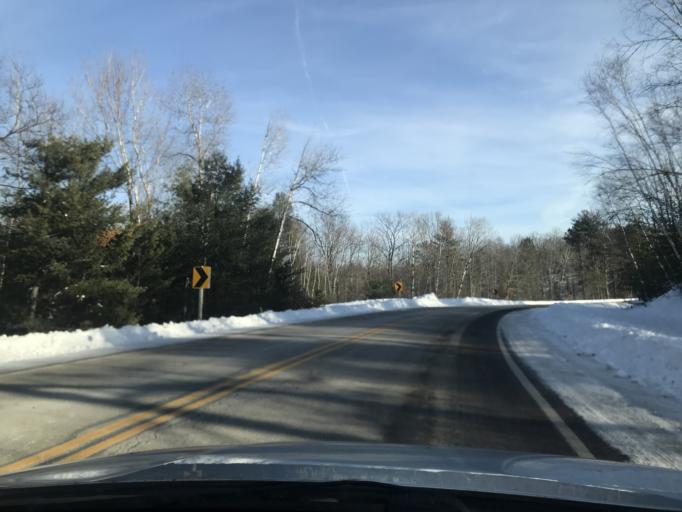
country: US
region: Wisconsin
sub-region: Menominee County
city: Keshena
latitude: 45.2591
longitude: -88.6379
